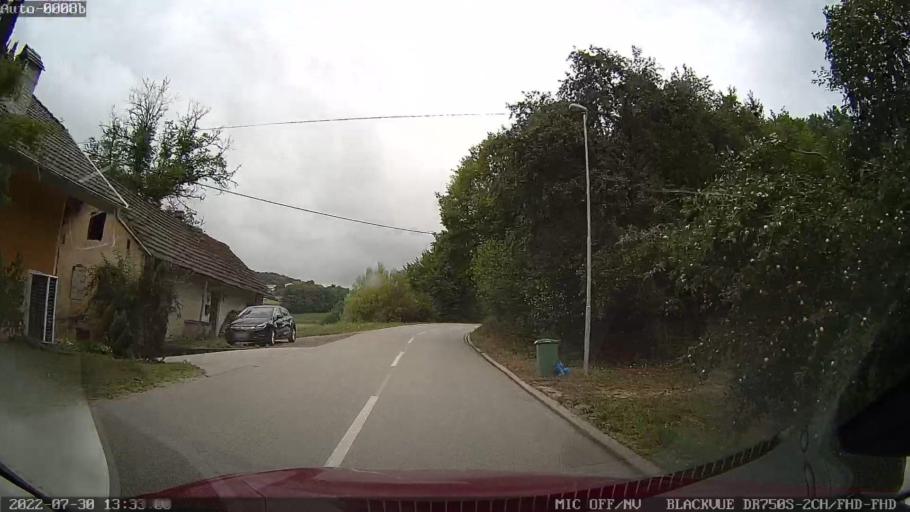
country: SI
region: Zuzemberk
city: Zuzemberk
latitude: 45.8483
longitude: 14.9365
